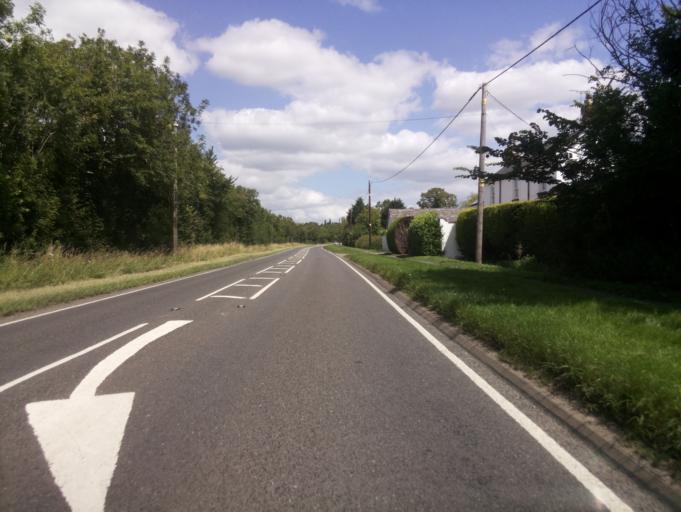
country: GB
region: England
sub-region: Buckinghamshire
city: Aylesbury
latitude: 51.8671
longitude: -0.8333
